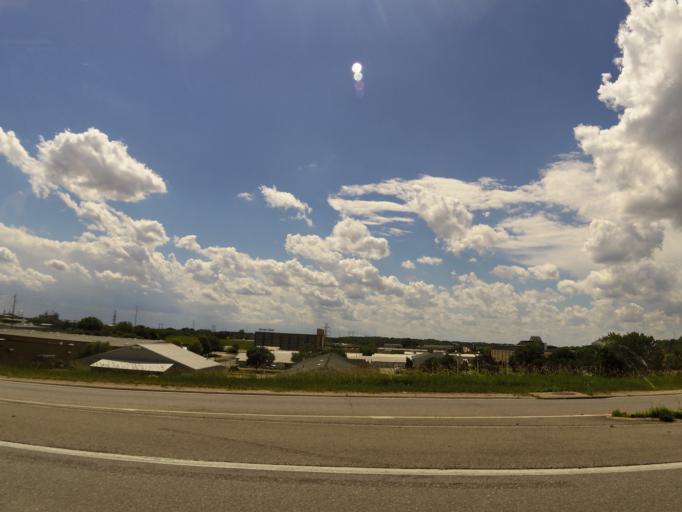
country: US
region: Iowa
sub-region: Linn County
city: Cedar Rapids
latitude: 41.9427
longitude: -91.6702
